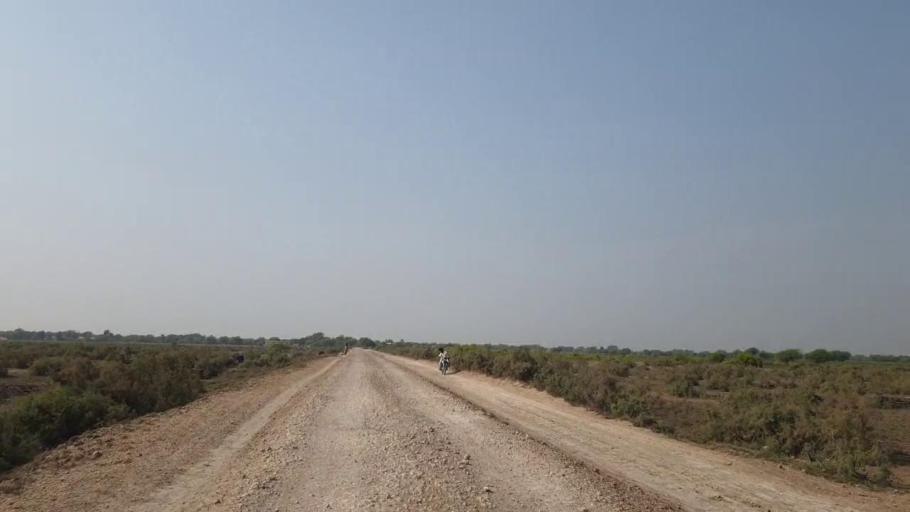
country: PK
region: Sindh
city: Kario
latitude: 24.9396
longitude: 68.5450
